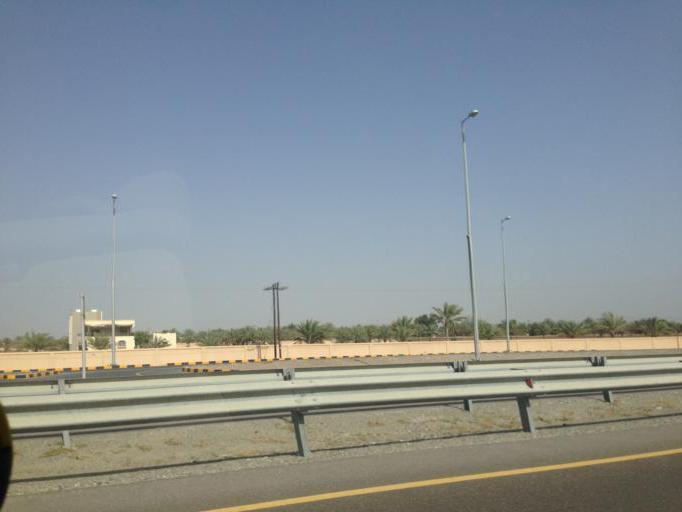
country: OM
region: Al Batinah
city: Barka'
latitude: 23.6527
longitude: 58.0279
